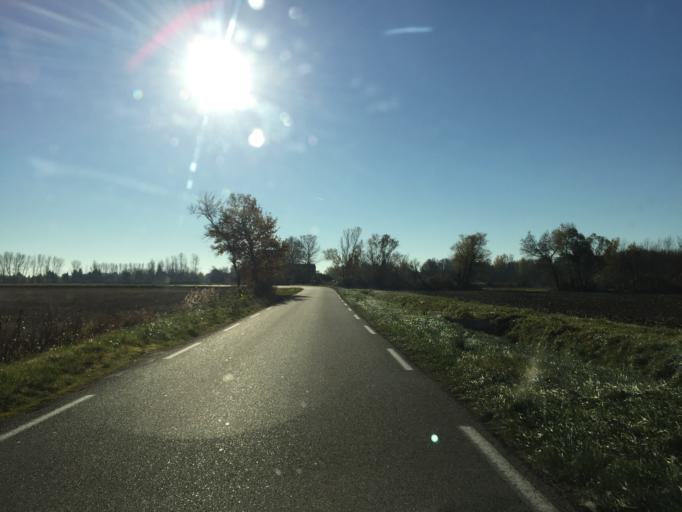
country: FR
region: Provence-Alpes-Cote d'Azur
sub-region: Departement du Vaucluse
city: Entraigues-sur-la-Sorgue
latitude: 44.0219
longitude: 4.9180
